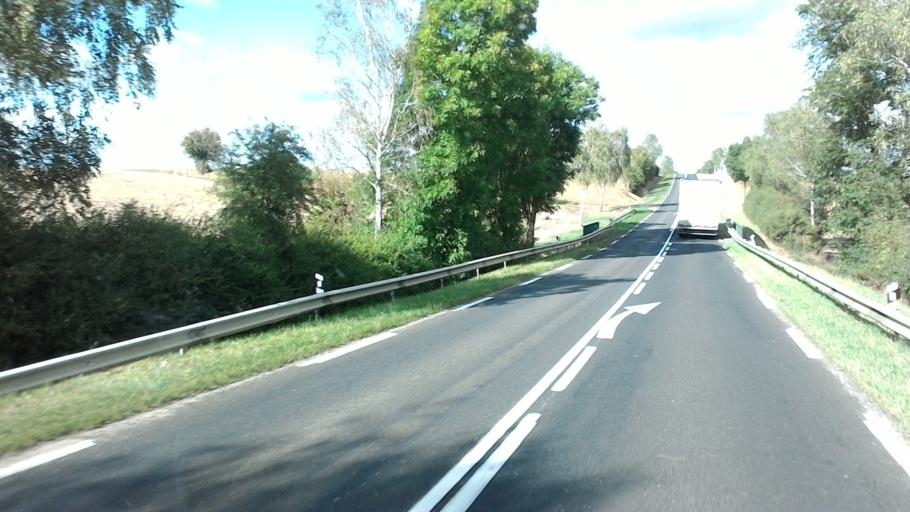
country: FR
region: Lorraine
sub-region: Departement de Meurthe-et-Moselle
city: Dommartin-les-Toul
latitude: 48.6283
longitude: 5.8916
